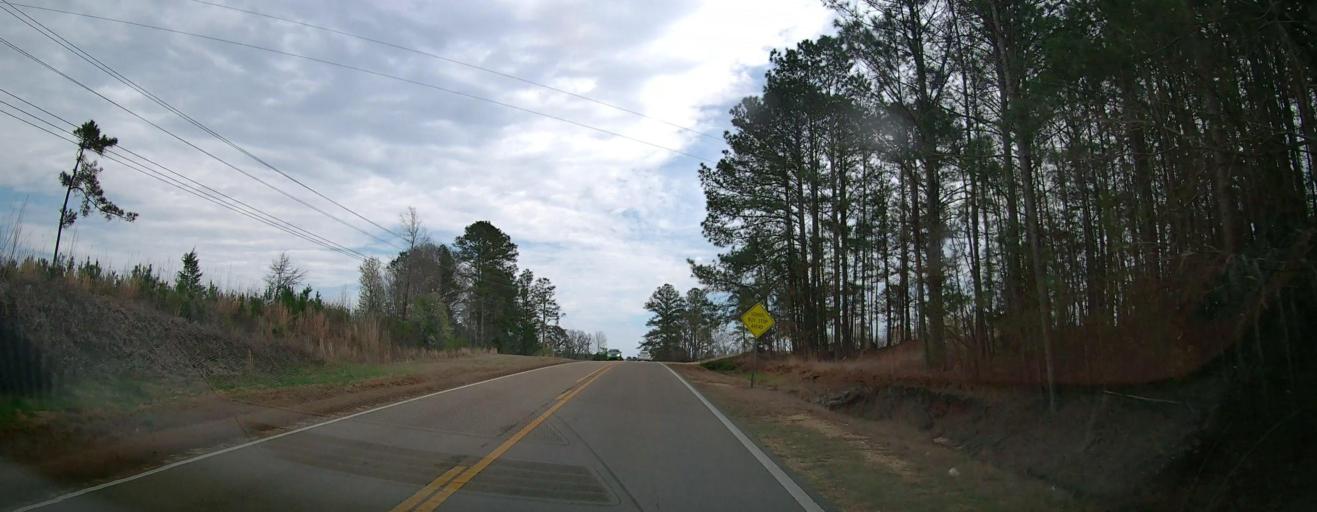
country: US
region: Mississippi
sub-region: Itawamba County
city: Fulton
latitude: 34.2769
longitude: -88.3604
